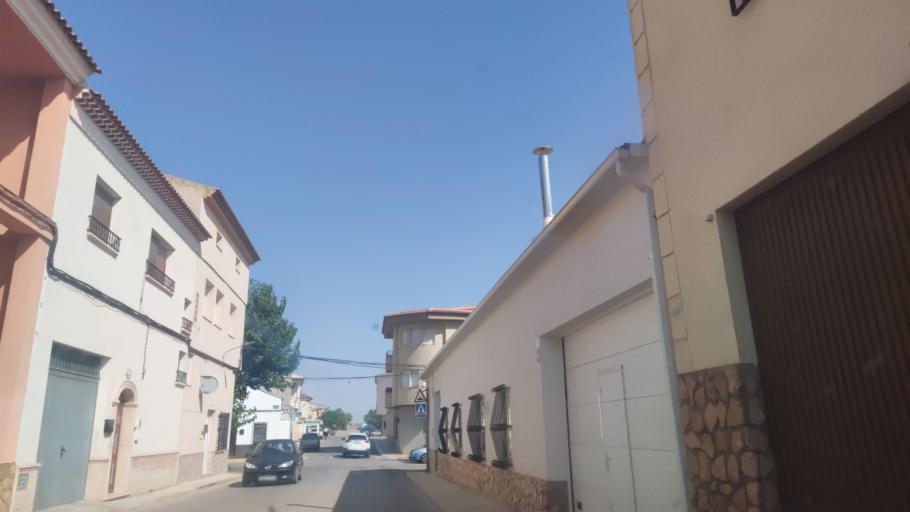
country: ES
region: Castille-La Mancha
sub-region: Provincia de Albacete
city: La Gineta
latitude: 39.1149
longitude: -1.9978
